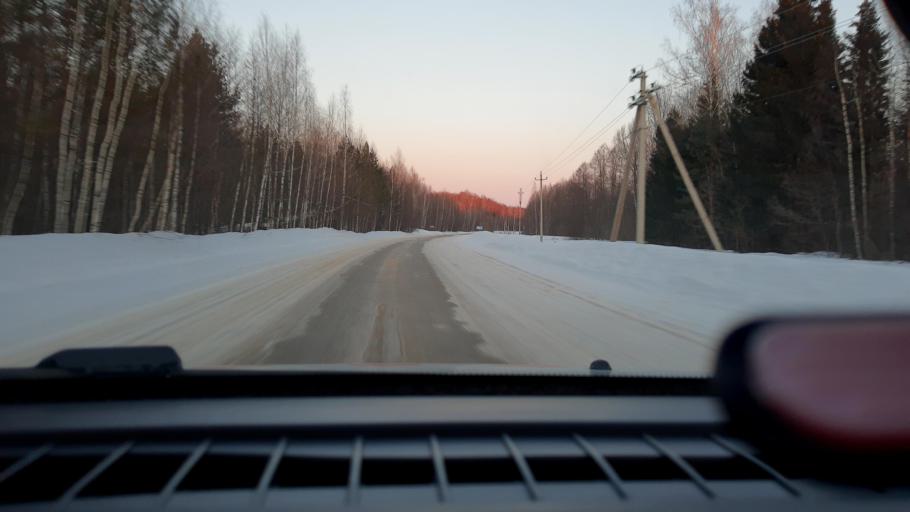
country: RU
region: Nizjnij Novgorod
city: Lyskovo
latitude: 56.1658
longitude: 45.2294
